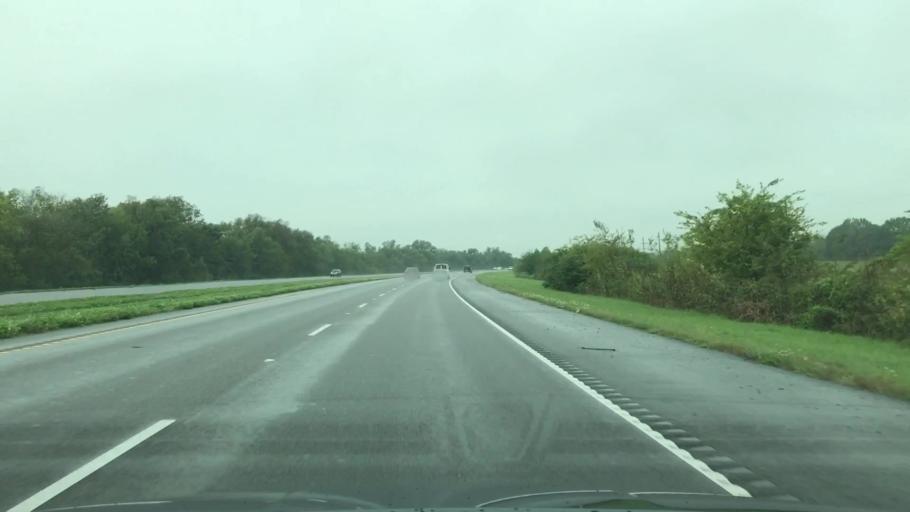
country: US
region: Louisiana
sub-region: Lafourche Parish
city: Raceland
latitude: 29.6915
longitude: -90.5906
